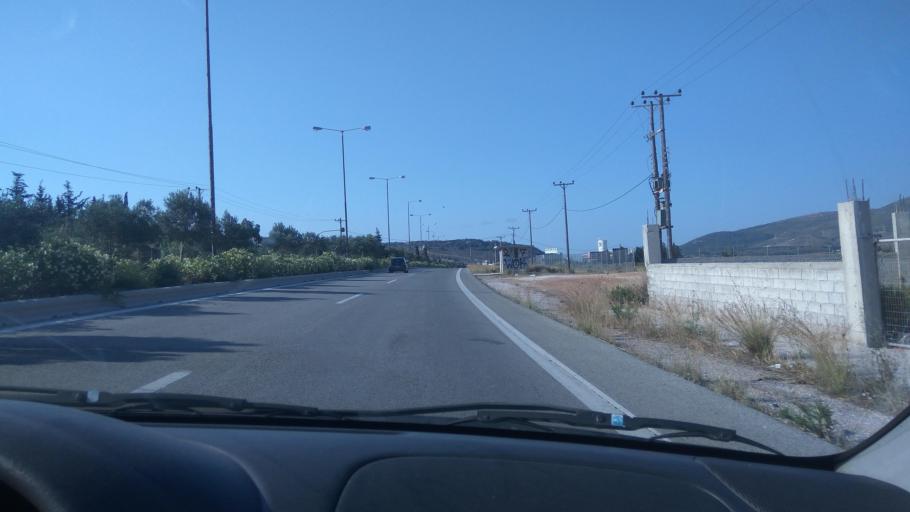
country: GR
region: Attica
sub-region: Nomarchia Anatolikis Attikis
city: Lavrio
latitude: 37.7919
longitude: 24.0565
